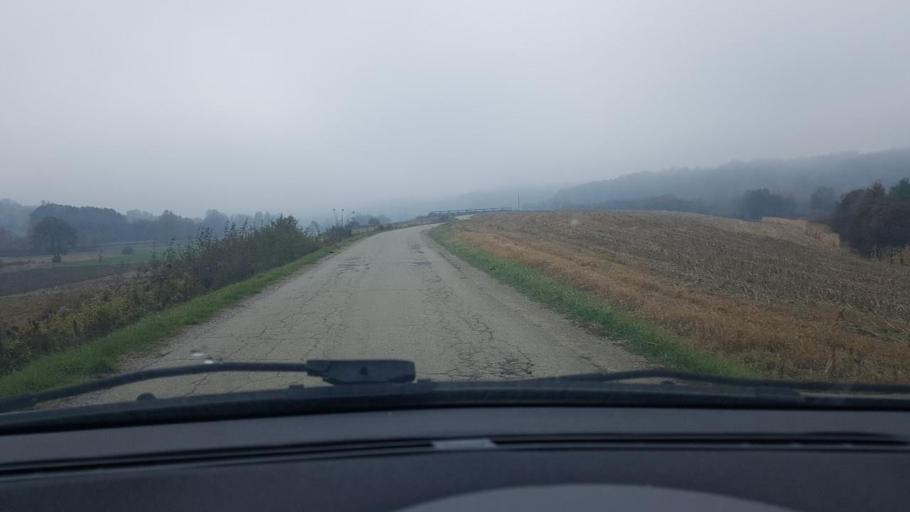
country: HR
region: Krapinsko-Zagorska
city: Zlatar
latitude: 46.1059
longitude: 16.1767
